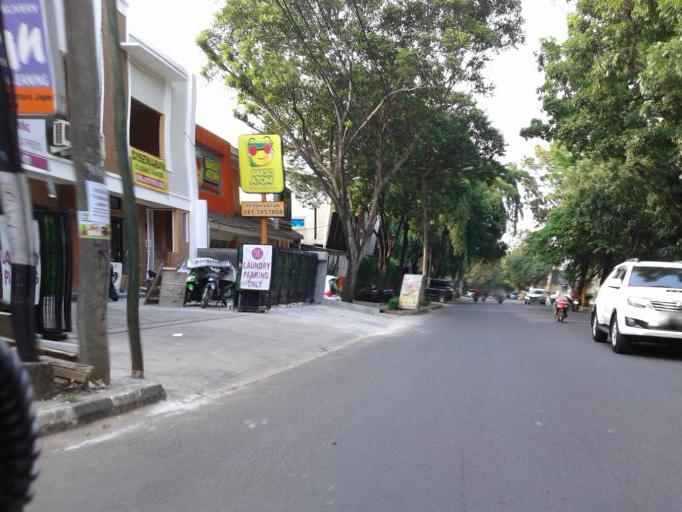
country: ID
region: Banten
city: South Tangerang
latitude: -6.2838
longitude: 106.7047
